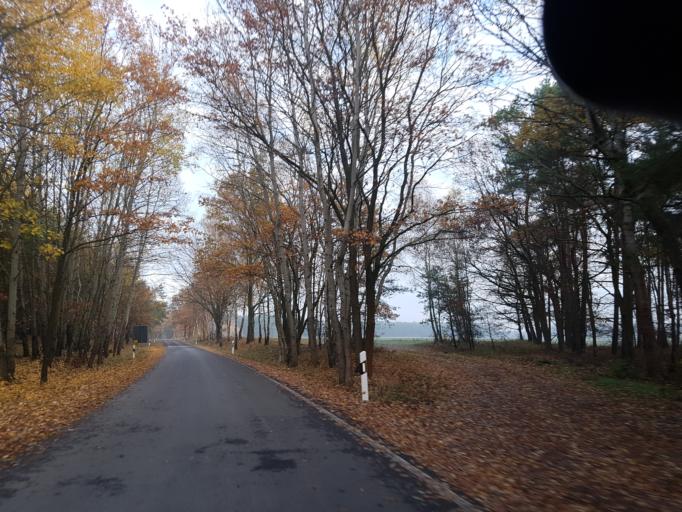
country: DE
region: Saxony-Anhalt
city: Abtsdorf
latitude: 51.9070
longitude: 12.7519
